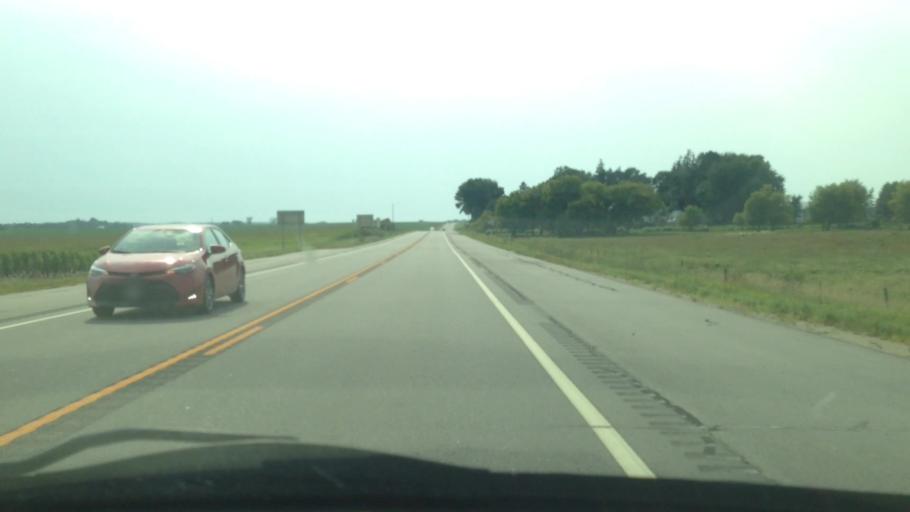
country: US
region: Minnesota
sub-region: Olmsted County
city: Eyota
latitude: 43.9991
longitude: -92.2543
